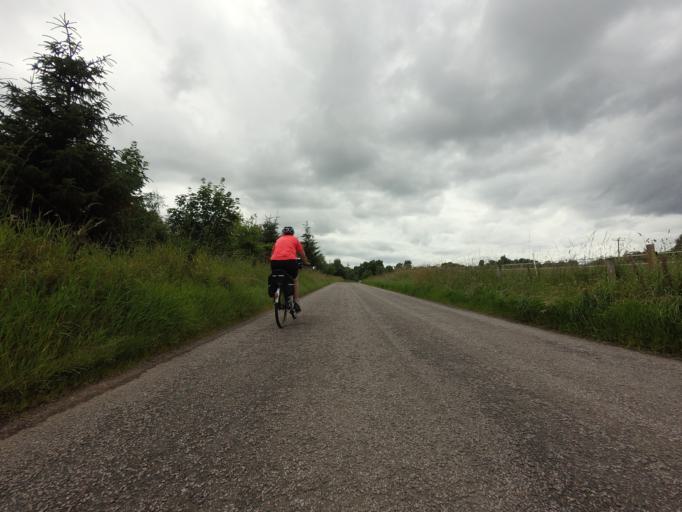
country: GB
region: Scotland
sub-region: Highland
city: Nairn
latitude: 57.5991
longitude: -3.8005
